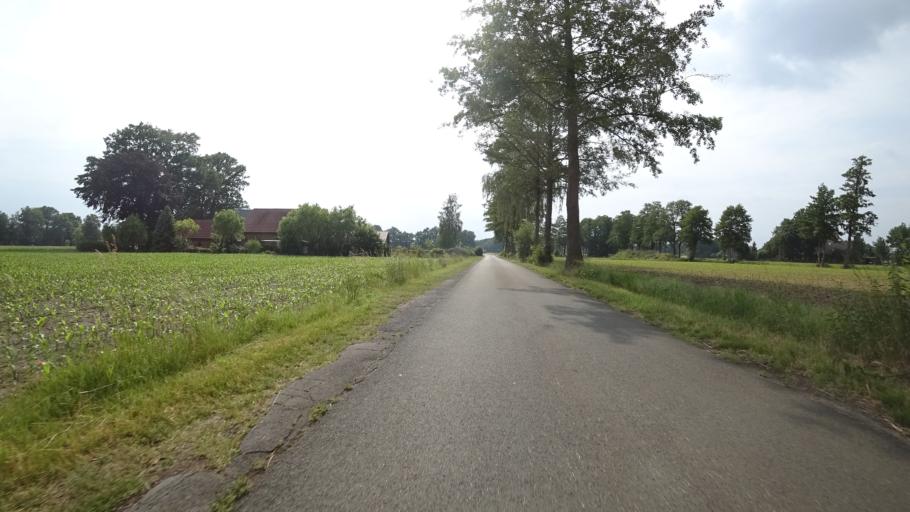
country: DE
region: North Rhine-Westphalia
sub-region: Regierungsbezirk Detmold
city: Guetersloh
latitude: 51.9484
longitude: 8.3762
